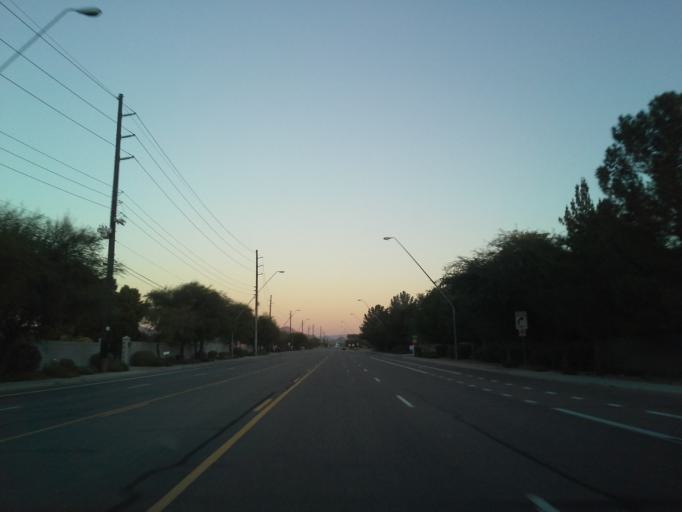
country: US
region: Arizona
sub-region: Maricopa County
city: Mesa
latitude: 33.4663
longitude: -111.7517
